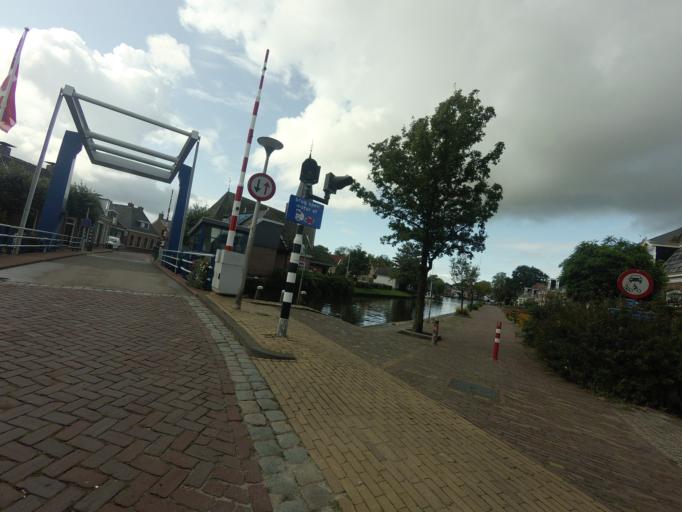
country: NL
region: Friesland
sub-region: Gemeente Boarnsterhim
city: Warten
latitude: 53.1500
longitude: 5.8979
